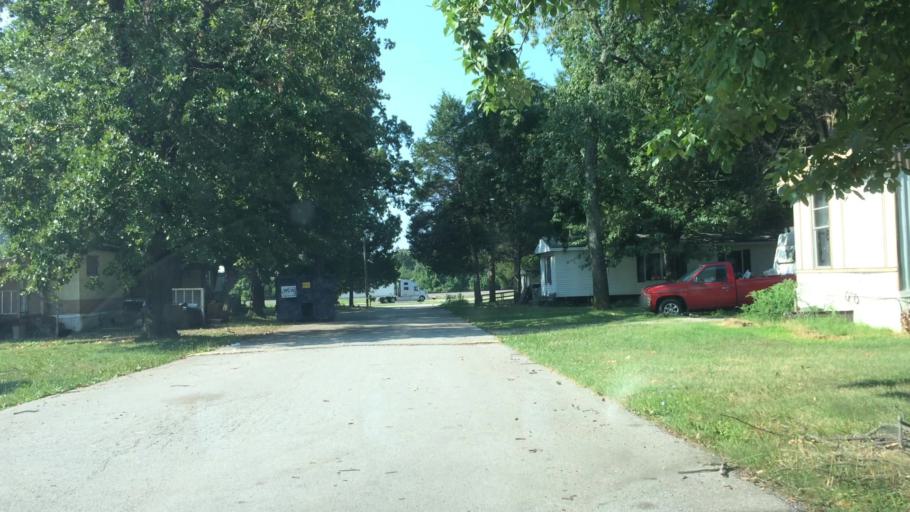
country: US
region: Missouri
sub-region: Greene County
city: Strafford
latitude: 37.2726
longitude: -93.0649
